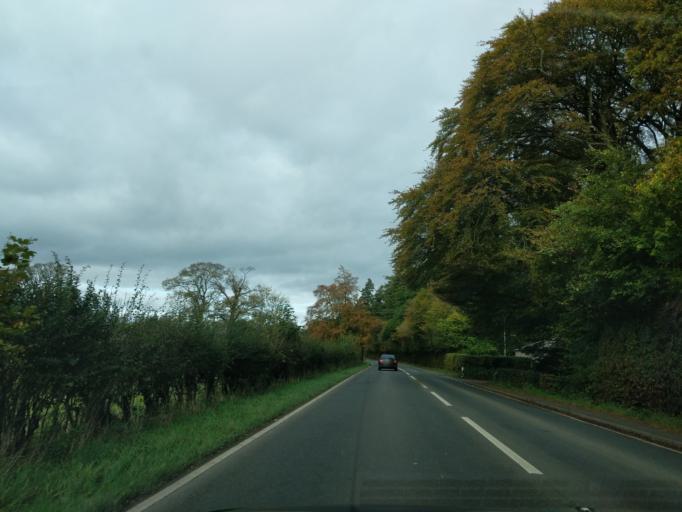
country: GB
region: Scotland
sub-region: Dumfries and Galloway
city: Thornhill
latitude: 55.2564
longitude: -3.7752
